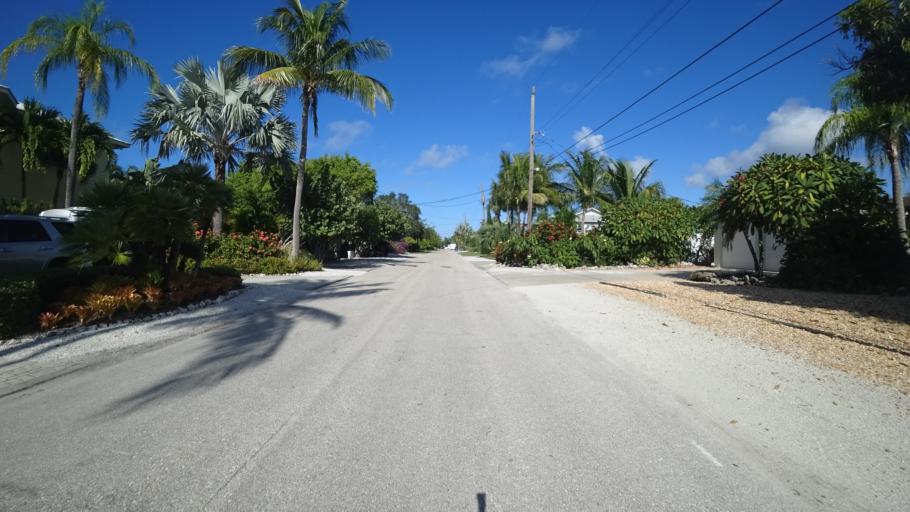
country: US
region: Florida
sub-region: Manatee County
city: Anna Maria
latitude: 27.5247
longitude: -82.7295
